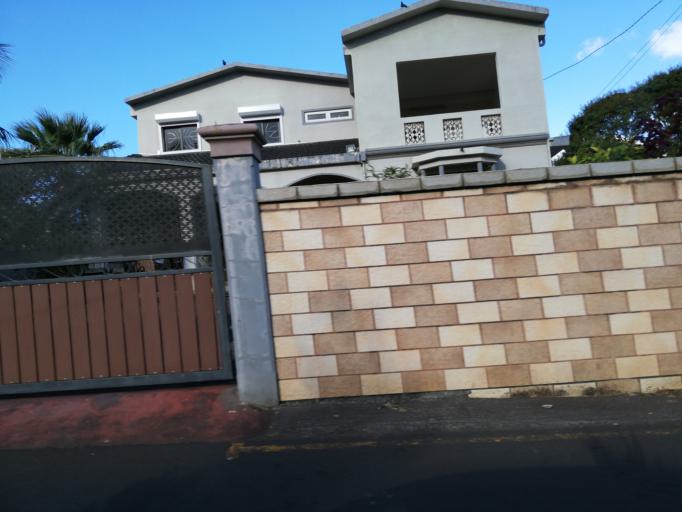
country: MU
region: Moka
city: Moka
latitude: -20.2225
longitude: 57.4755
